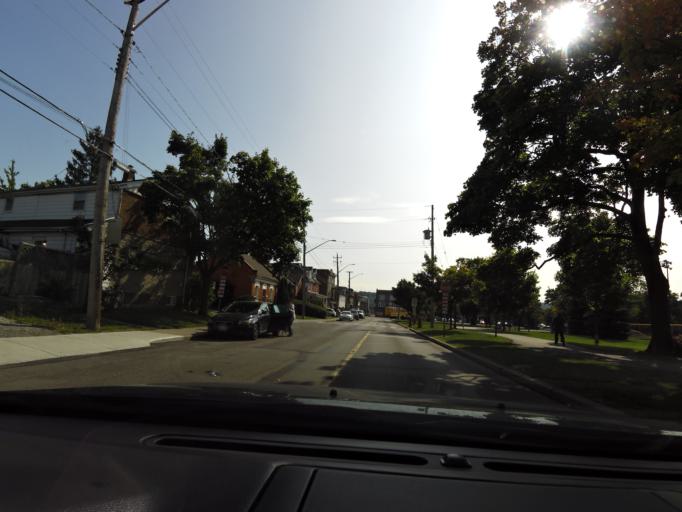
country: CA
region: Ontario
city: Hamilton
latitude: 43.2618
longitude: -79.8830
